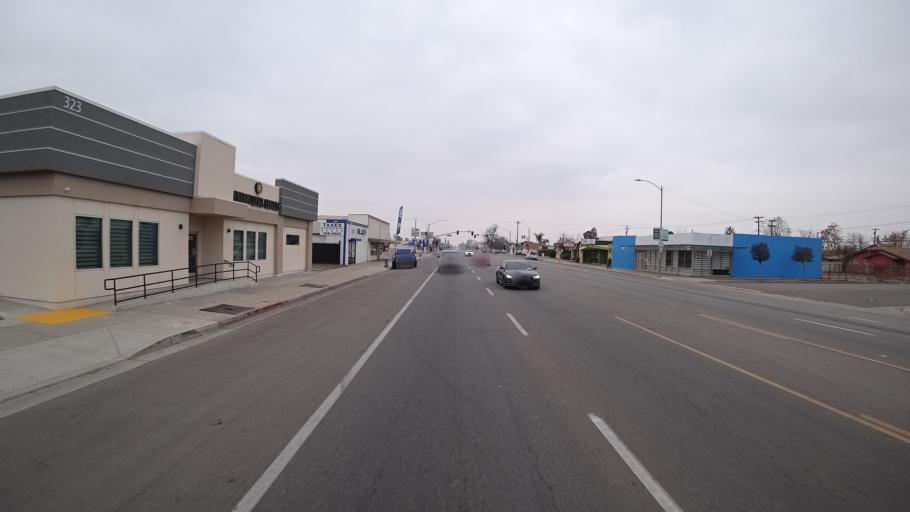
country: US
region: California
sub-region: Kern County
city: Bakersfield
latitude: 35.3597
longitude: -119.0190
